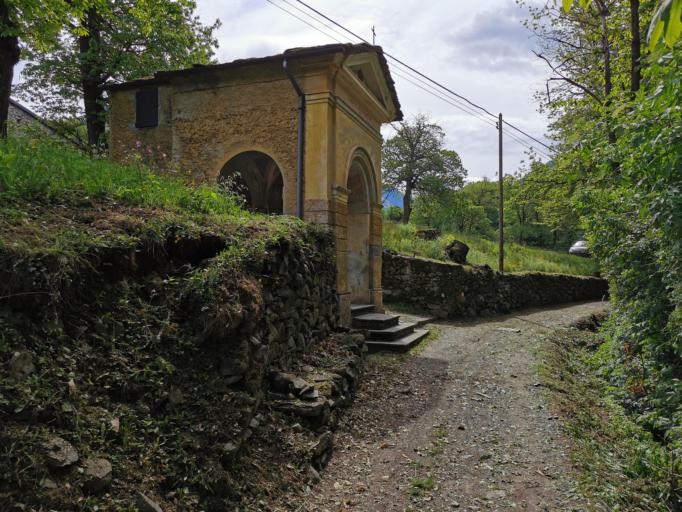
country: IT
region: Lombardy
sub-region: Provincia di Sondrio
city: Bema
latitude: 46.1224
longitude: 9.5610
